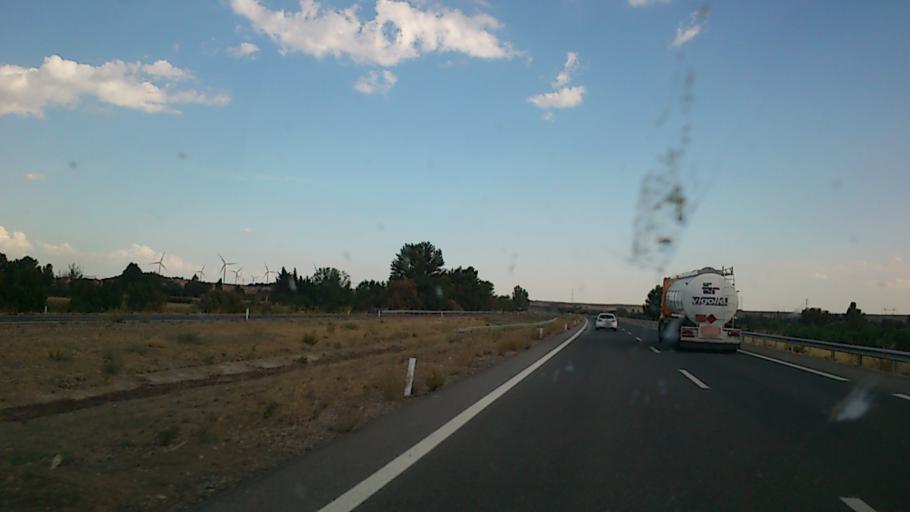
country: ES
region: Aragon
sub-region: Provincia de Zaragoza
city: Frescano
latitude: 41.8976
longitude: -1.4388
